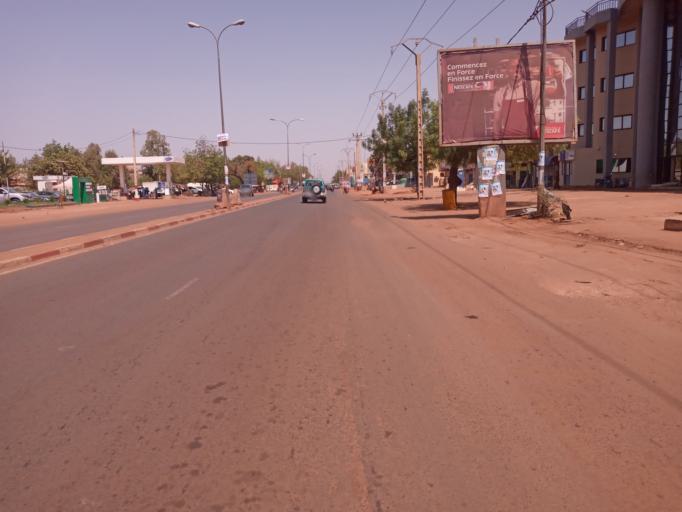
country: ML
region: Bamako
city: Bamako
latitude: 12.6638
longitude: -7.9437
